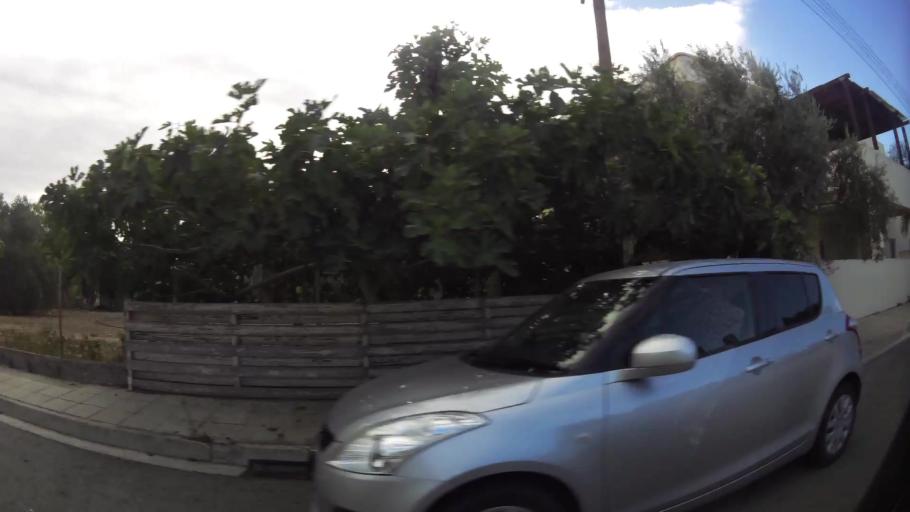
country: CY
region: Lefkosia
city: Nicosia
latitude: 35.1461
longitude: 33.3353
